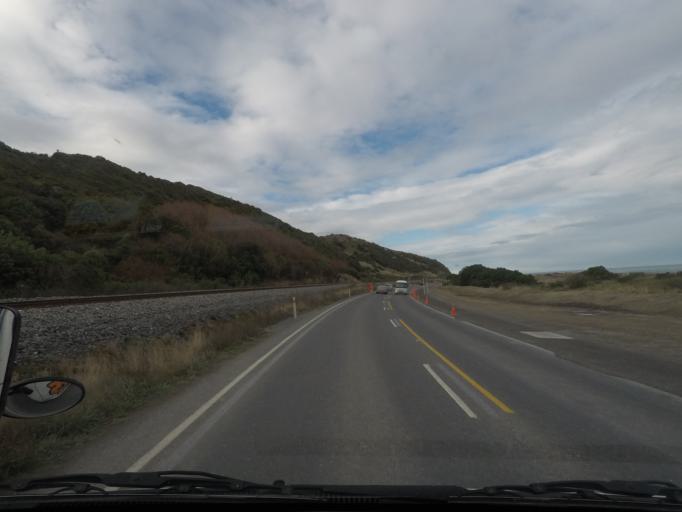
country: NZ
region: Canterbury
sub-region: Kaikoura District
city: Kaikoura
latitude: -42.2163
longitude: 173.8623
